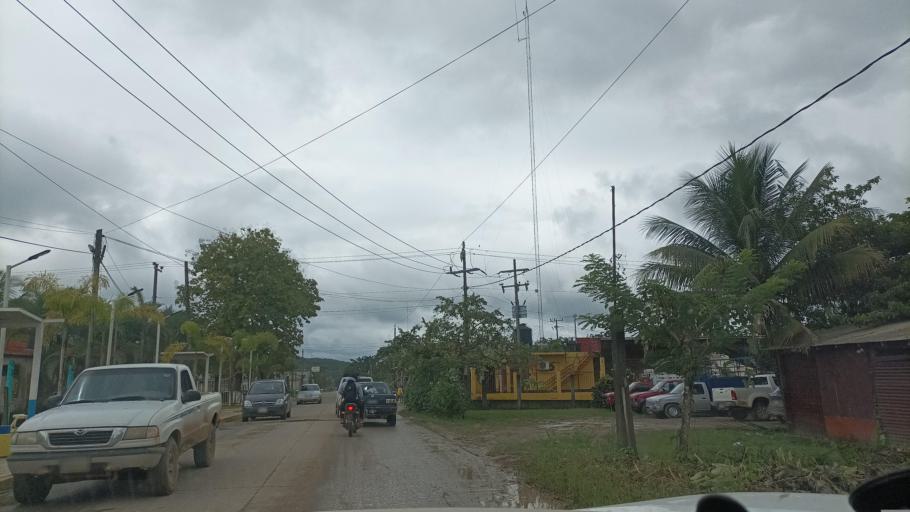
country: MX
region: Veracruz
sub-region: Uxpanapa
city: Poblado 10
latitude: 17.2796
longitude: -94.4550
